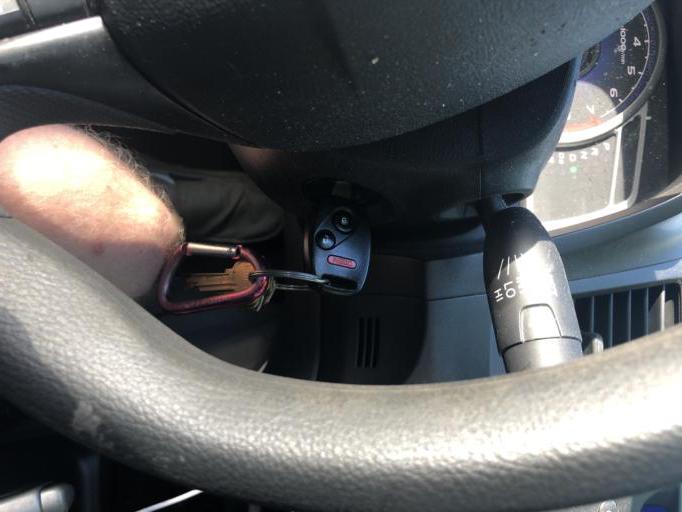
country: US
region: Tennessee
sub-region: Davidson County
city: Forest Hills
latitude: 36.0749
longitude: -86.8218
